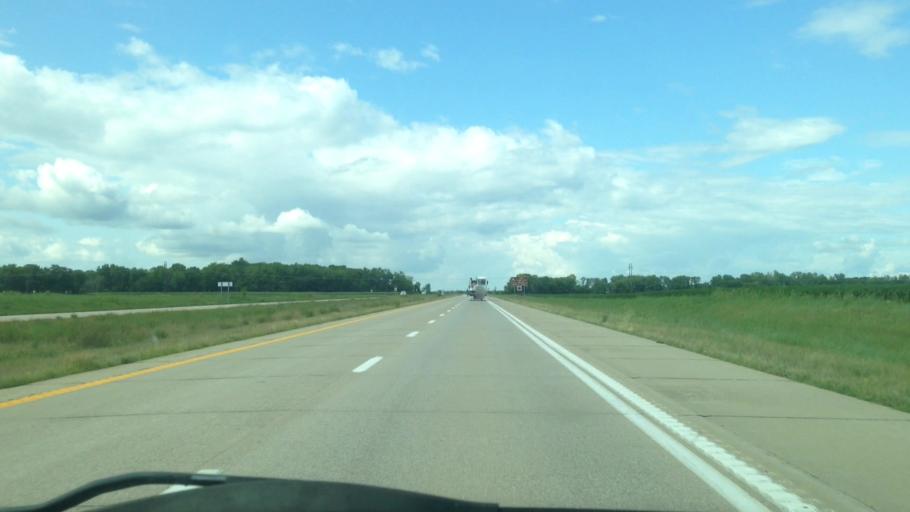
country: US
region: Missouri
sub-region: Clark County
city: Kahoka
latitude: 40.4244
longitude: -91.5715
